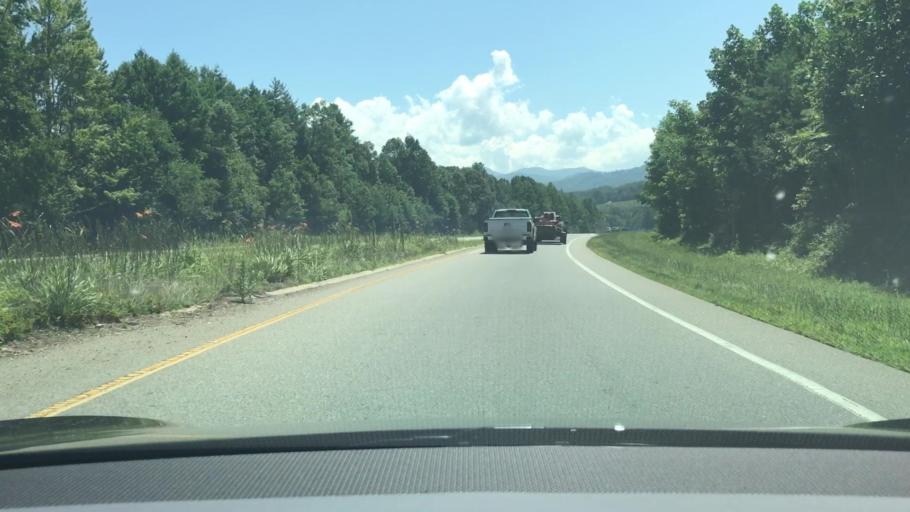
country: US
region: North Carolina
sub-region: Macon County
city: Franklin
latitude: 35.1655
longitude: -83.3859
